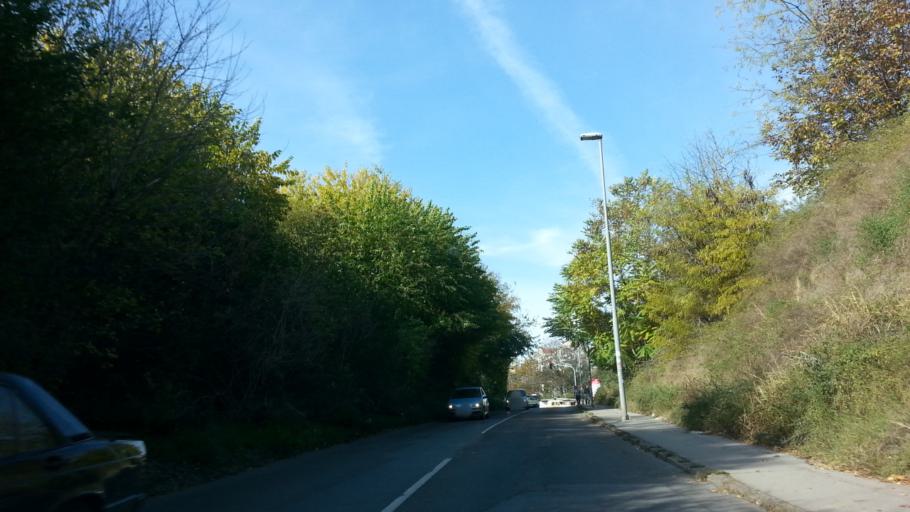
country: RS
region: Central Serbia
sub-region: Belgrade
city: Zemun
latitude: 44.8126
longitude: 20.3806
